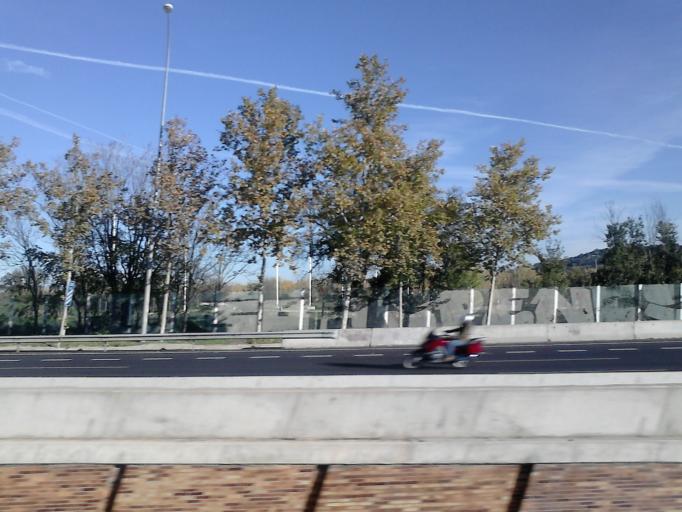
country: ES
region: Madrid
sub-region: Provincia de Madrid
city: Moncloa-Aravaca
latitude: 40.4598
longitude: -3.7517
